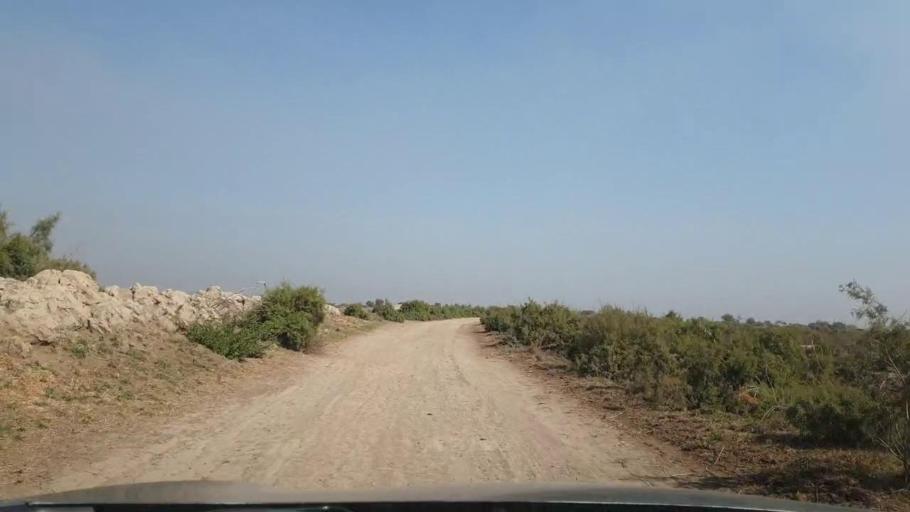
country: PK
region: Sindh
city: Berani
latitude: 25.6566
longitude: 68.8816
